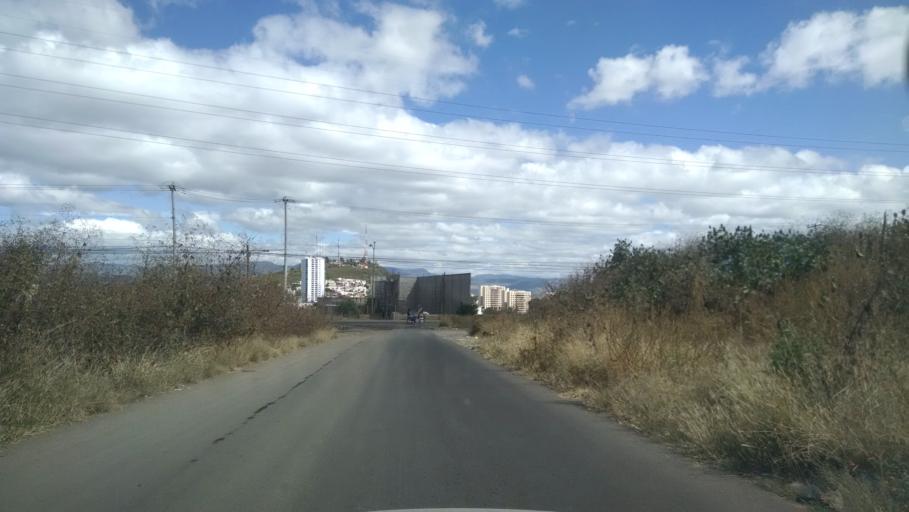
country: MX
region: Guanajuato
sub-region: Leon
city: La Ermita
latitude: 21.1565
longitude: -101.7321
